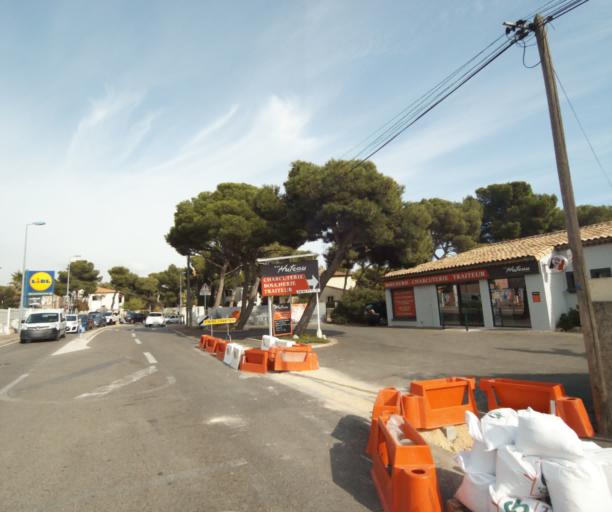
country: FR
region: Provence-Alpes-Cote d'Azur
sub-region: Departement des Bouches-du-Rhone
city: Sausset-les-Pins
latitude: 43.3320
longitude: 5.1241
